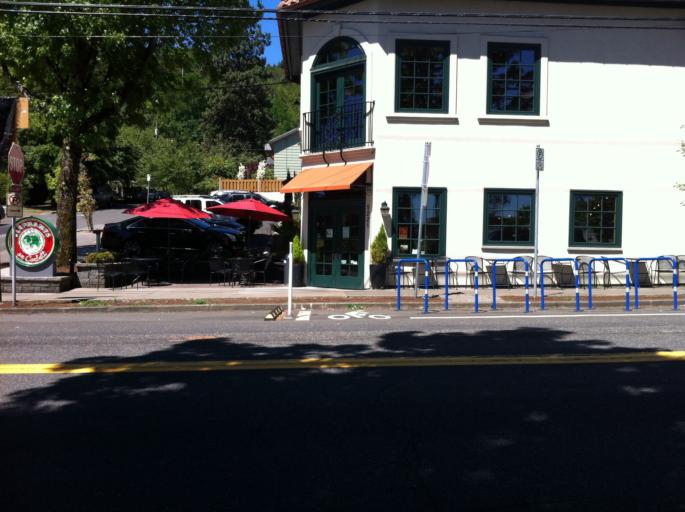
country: US
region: Oregon
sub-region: Multnomah County
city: Portland
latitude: 45.4851
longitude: -122.6767
